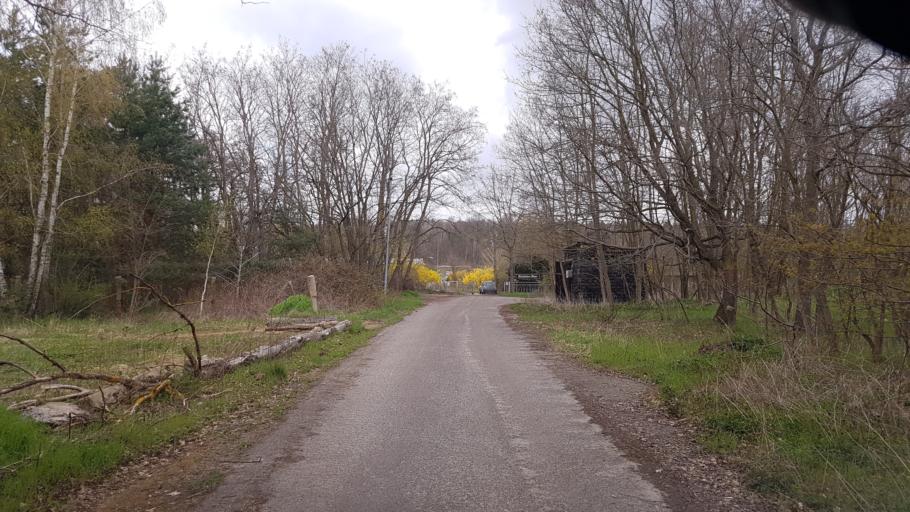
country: DE
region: Brandenburg
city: Plessa
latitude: 51.4736
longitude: 13.6074
